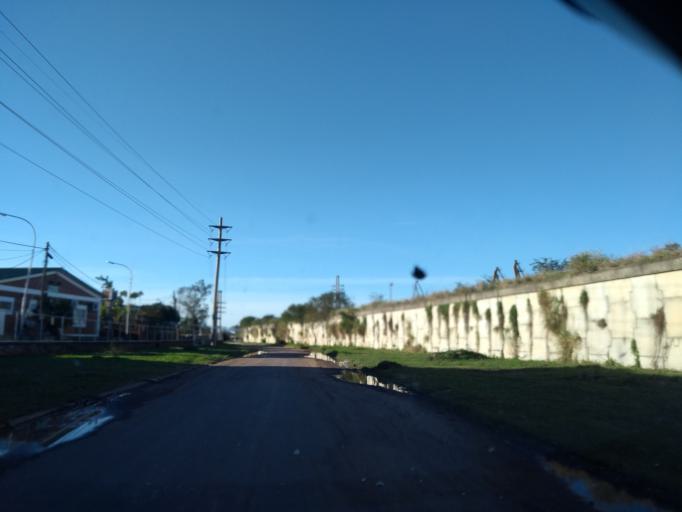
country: AR
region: Chaco
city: Barranqueras
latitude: -27.4926
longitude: -58.9281
